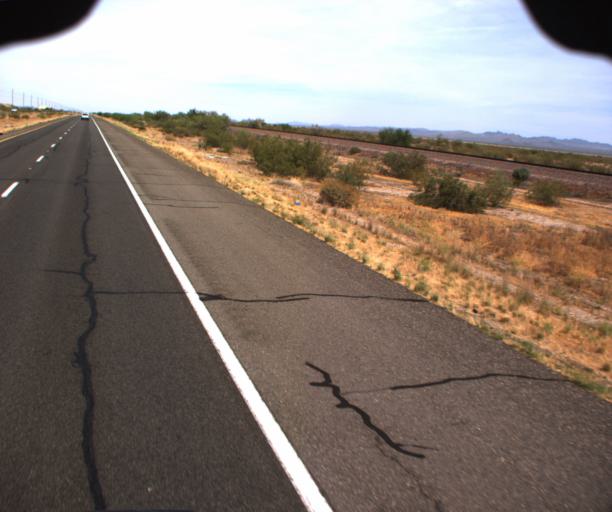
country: US
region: Arizona
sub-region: Maricopa County
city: Sun City West
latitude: 33.7287
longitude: -112.4654
